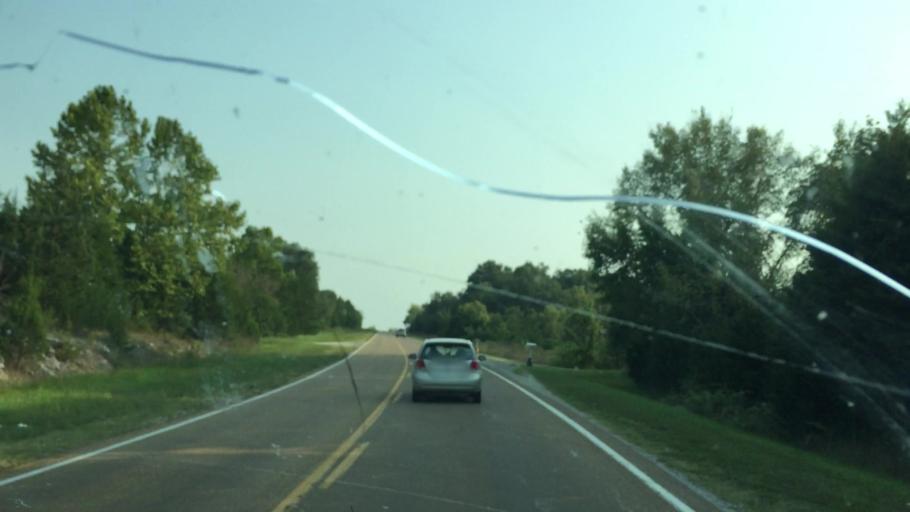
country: US
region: Missouri
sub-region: Pulaski County
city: Richland
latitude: 37.8168
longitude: -92.4073
